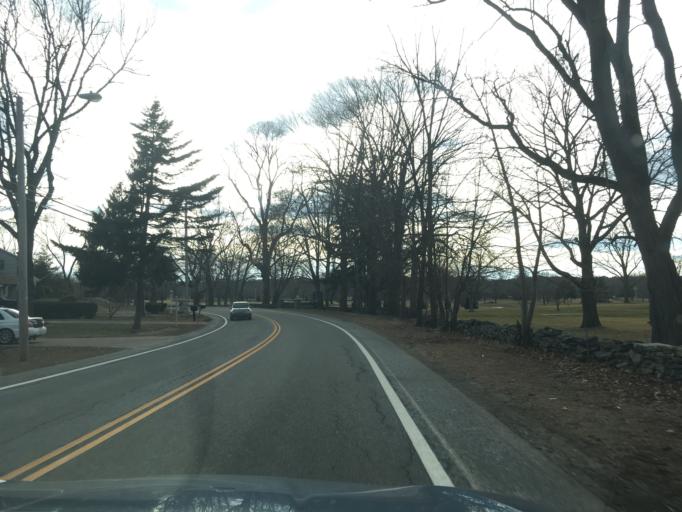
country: US
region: Rhode Island
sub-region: Kent County
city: East Greenwich
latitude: 41.6602
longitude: -71.4241
